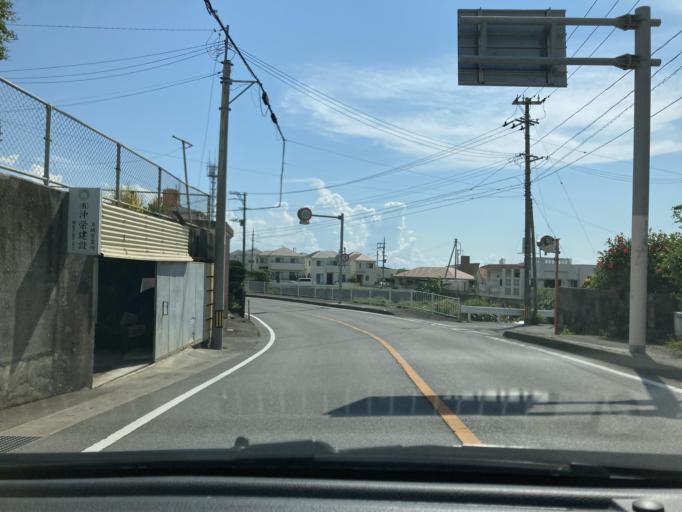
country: JP
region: Okinawa
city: Tomigusuku
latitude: 26.1428
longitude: 127.7929
